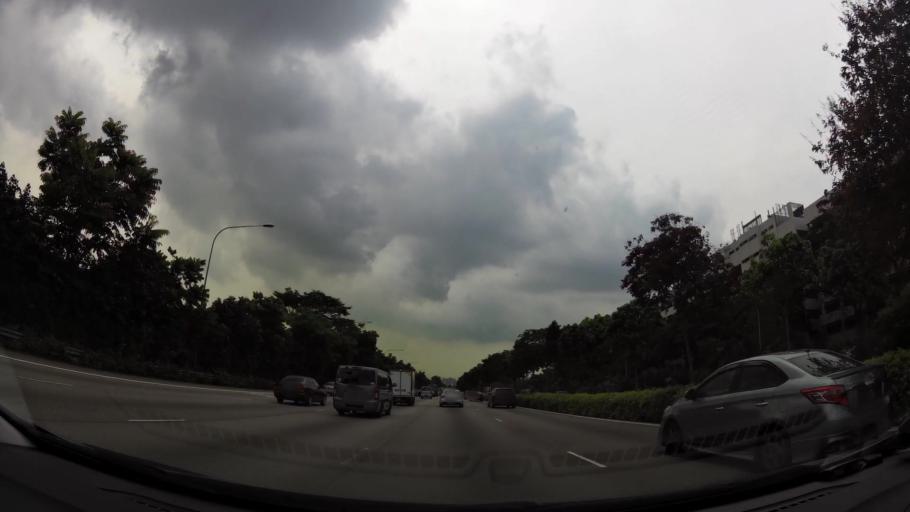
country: SG
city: Singapore
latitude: 1.3605
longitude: 103.8582
